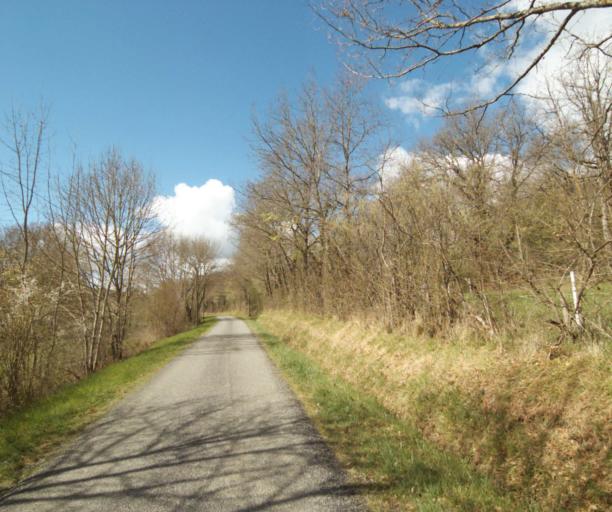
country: FR
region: Midi-Pyrenees
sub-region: Departement de l'Ariege
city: Saverdun
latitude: 43.1824
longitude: 1.5548
